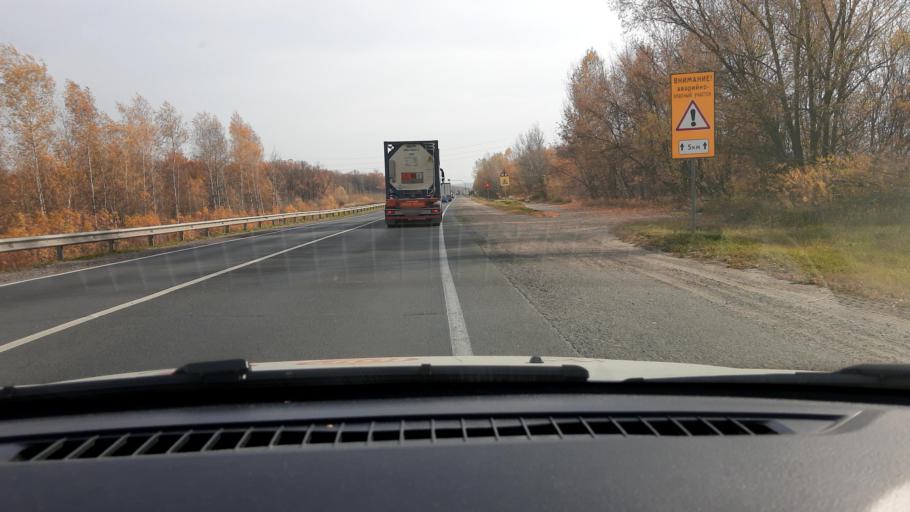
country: RU
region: Nizjnij Novgorod
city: Kstovo
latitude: 56.0943
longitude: 44.3198
